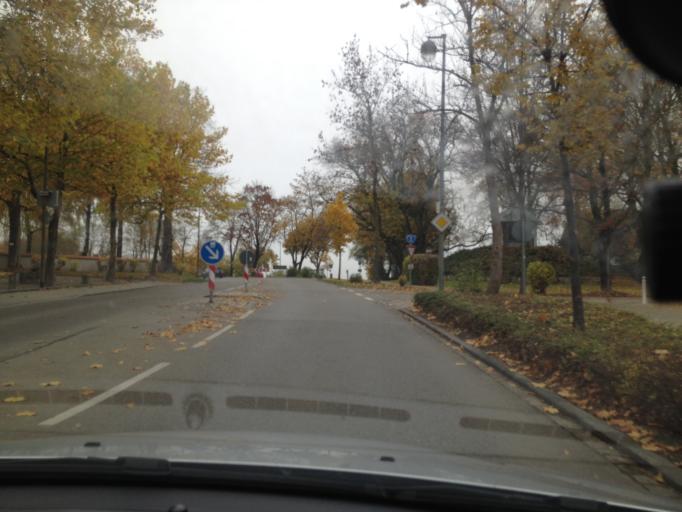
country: DE
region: Bavaria
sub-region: Swabia
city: Untermeitingen
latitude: 48.1630
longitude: 10.8049
